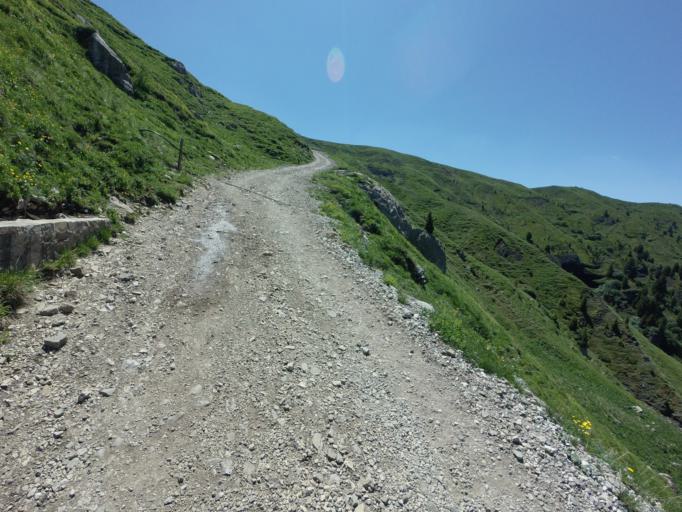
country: IT
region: Trentino-Alto Adige
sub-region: Provincia di Trento
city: Mazzin
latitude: 46.5075
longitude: 11.6972
